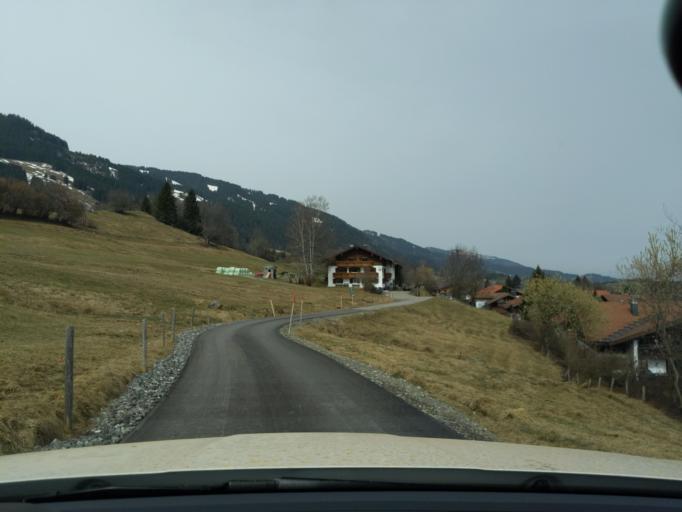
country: DE
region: Bavaria
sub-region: Swabia
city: Obermaiselstein
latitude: 47.4445
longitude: 10.2356
